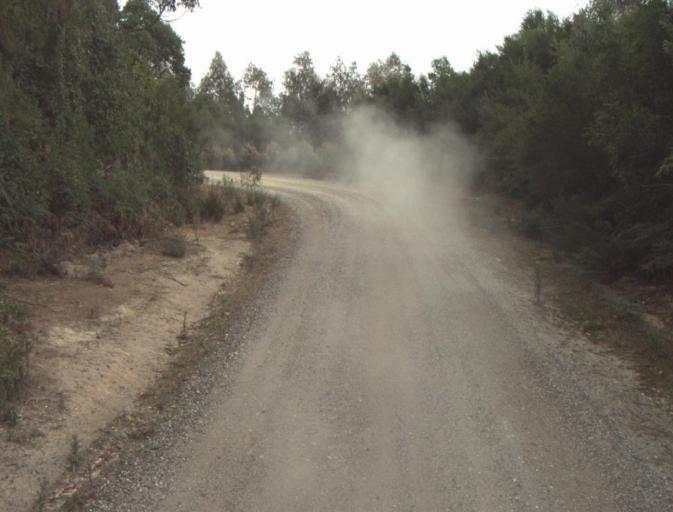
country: AU
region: Tasmania
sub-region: Launceston
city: Mayfield
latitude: -41.1580
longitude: 147.1718
